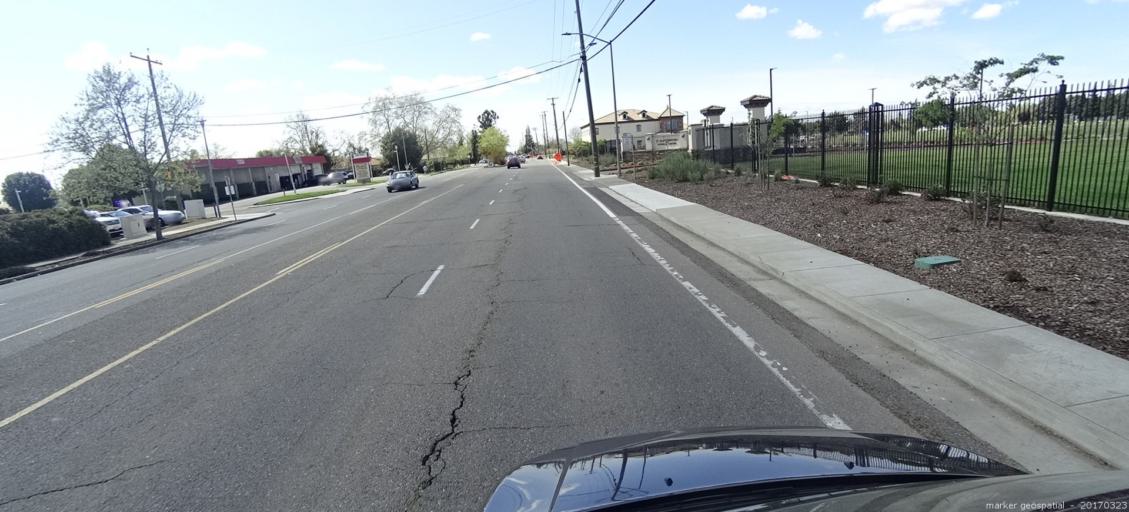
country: US
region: California
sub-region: Sacramento County
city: Florin
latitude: 38.5251
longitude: -121.4248
